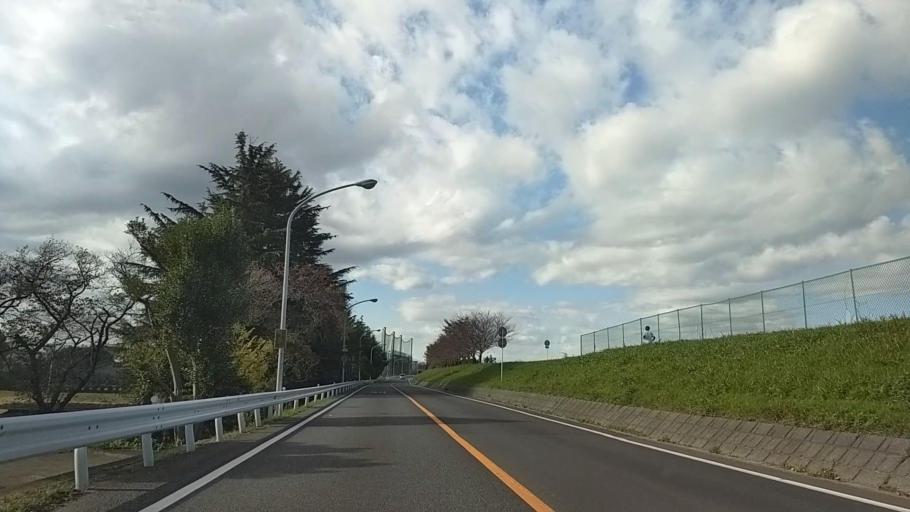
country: JP
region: Kanagawa
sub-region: Kawasaki-shi
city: Kawasaki
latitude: 35.5880
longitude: 139.6581
